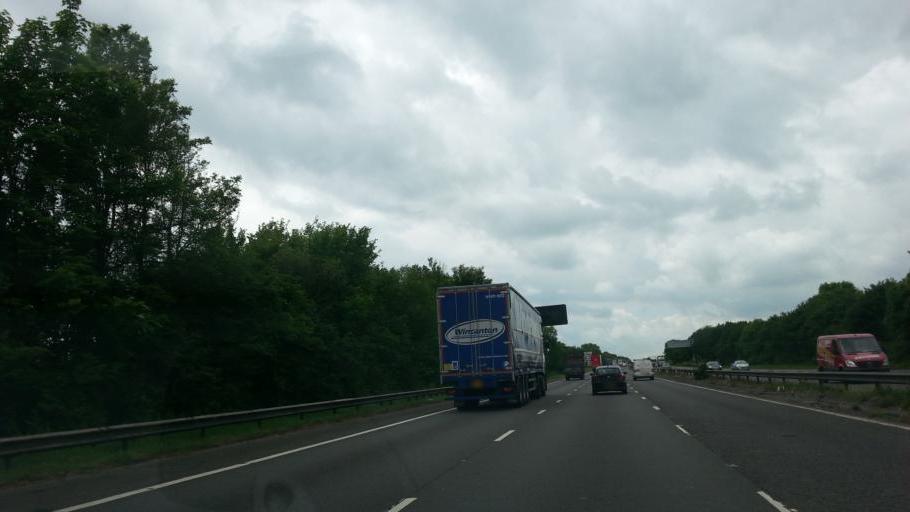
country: GB
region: England
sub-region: Solihull
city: Meriden
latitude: 52.4673
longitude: -1.6052
